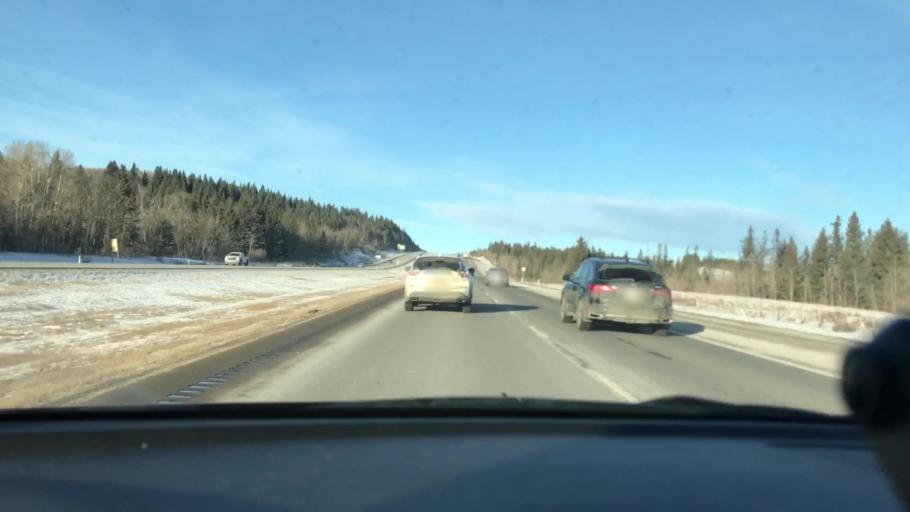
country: CA
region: Alberta
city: Cochrane
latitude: 51.1325
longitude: -114.6974
